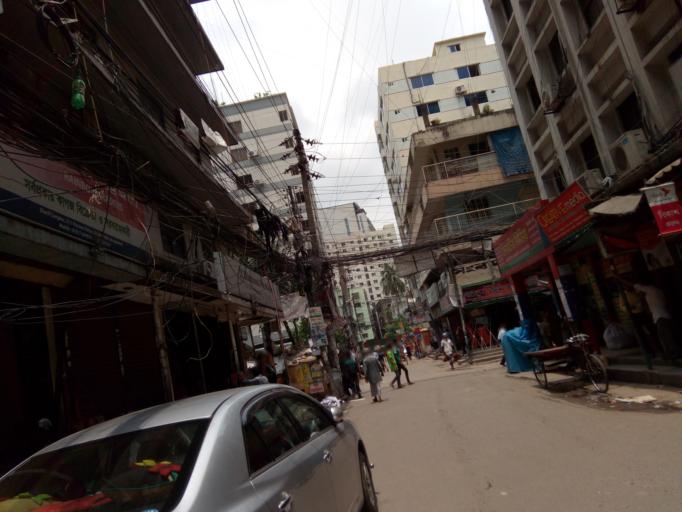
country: BD
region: Dhaka
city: Paltan
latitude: 23.7317
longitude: 90.4115
